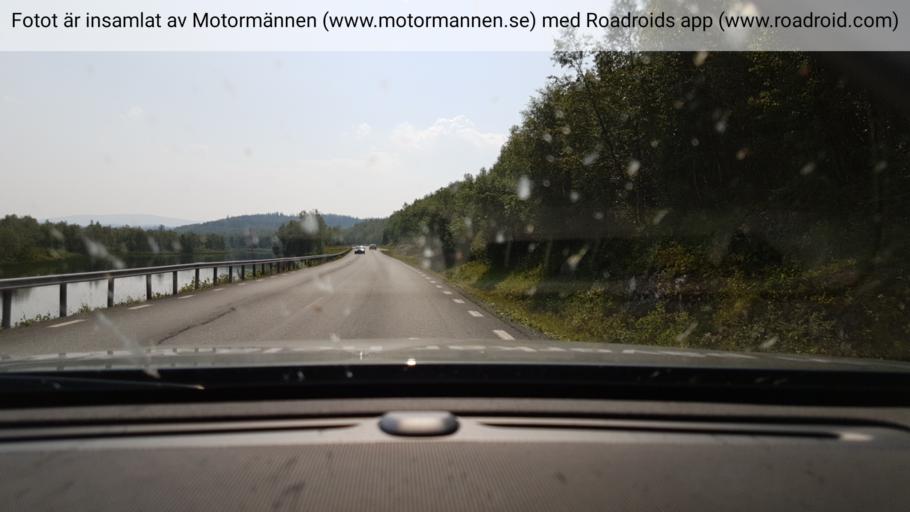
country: NO
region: Nordland
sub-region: Rana
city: Mo i Rana
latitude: 65.7305
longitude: 15.1696
